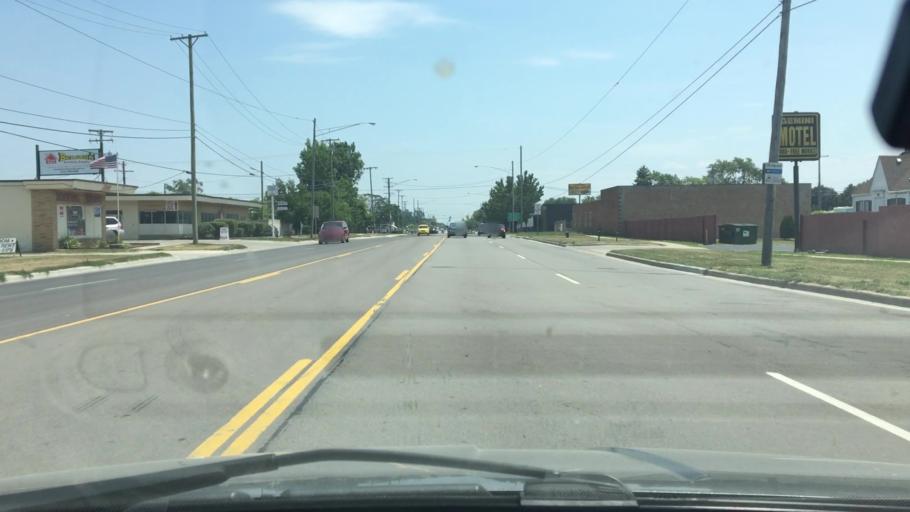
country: US
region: Michigan
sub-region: Wayne County
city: Redford
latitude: 42.3710
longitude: -83.2863
